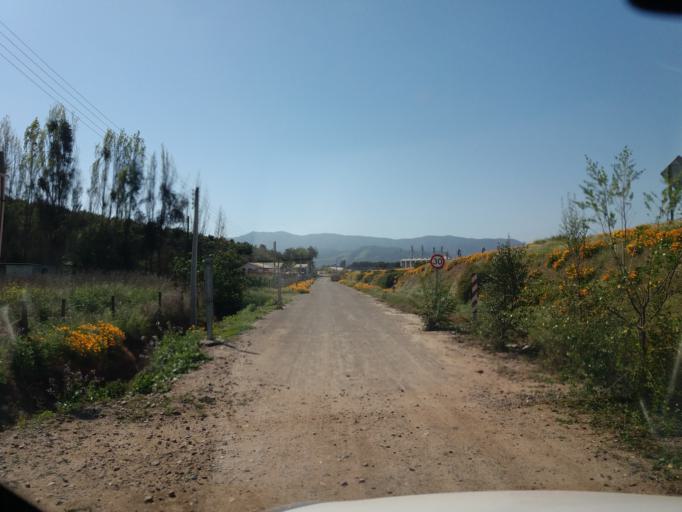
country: CL
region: Valparaiso
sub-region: Provincia de Marga Marga
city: Limache
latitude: -32.9489
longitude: -71.2856
